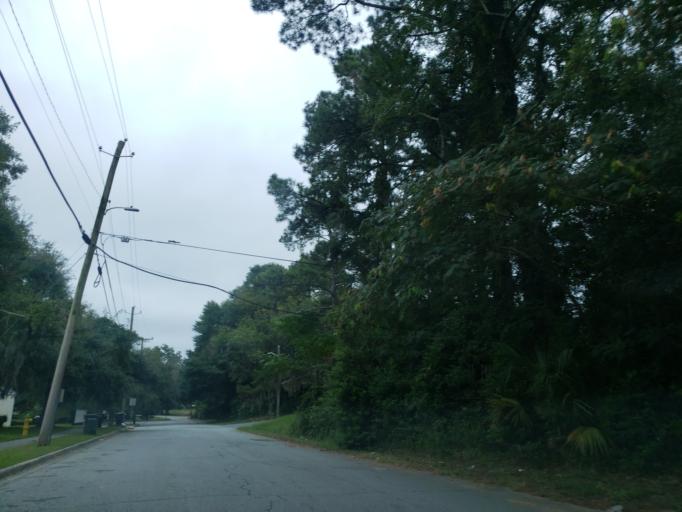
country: US
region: Georgia
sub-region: Chatham County
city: Thunderbolt
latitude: 32.0489
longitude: -81.0731
